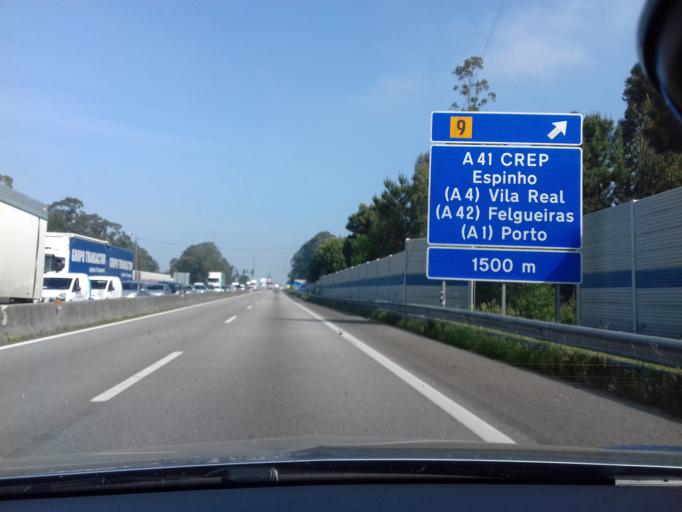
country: PT
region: Aveiro
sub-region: Espinho
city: Souto
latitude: 40.9932
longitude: -8.6155
